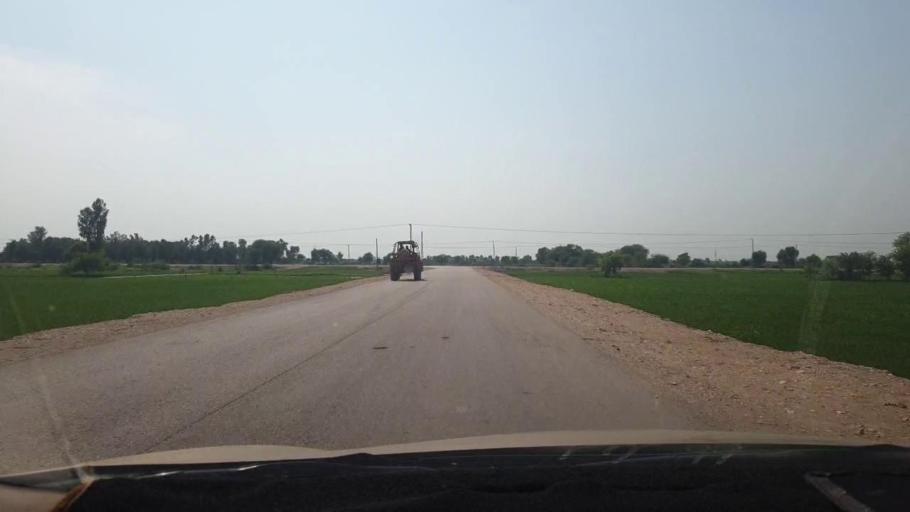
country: PK
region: Sindh
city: Larkana
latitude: 27.6112
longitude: 68.2353
